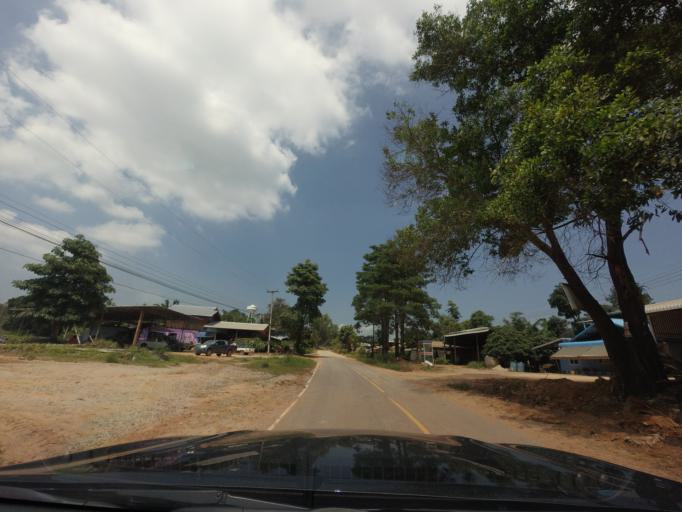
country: TH
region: Loei
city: Na Haeo
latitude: 17.5213
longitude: 100.8800
